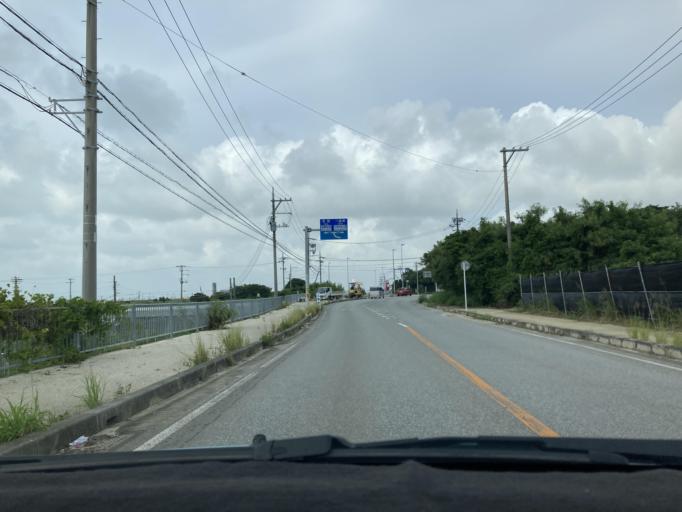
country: JP
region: Okinawa
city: Itoman
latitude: 26.1107
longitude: 127.6682
